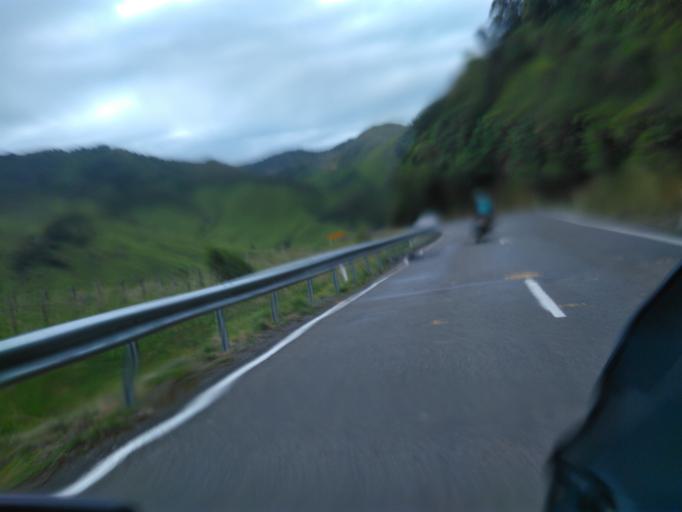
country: NZ
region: Bay of Plenty
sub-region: Opotiki District
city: Opotiki
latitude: -38.3603
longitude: 177.4558
